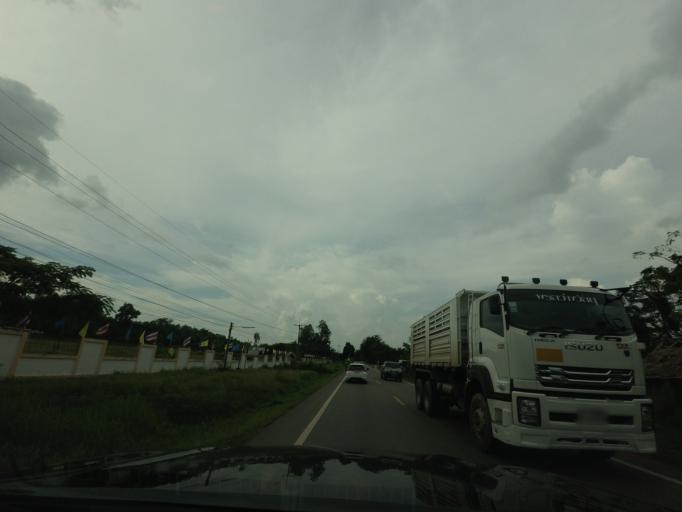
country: TH
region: Changwat Nong Bua Lamphu
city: Nong Bua Lamphu
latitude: 17.3326
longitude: 102.3851
